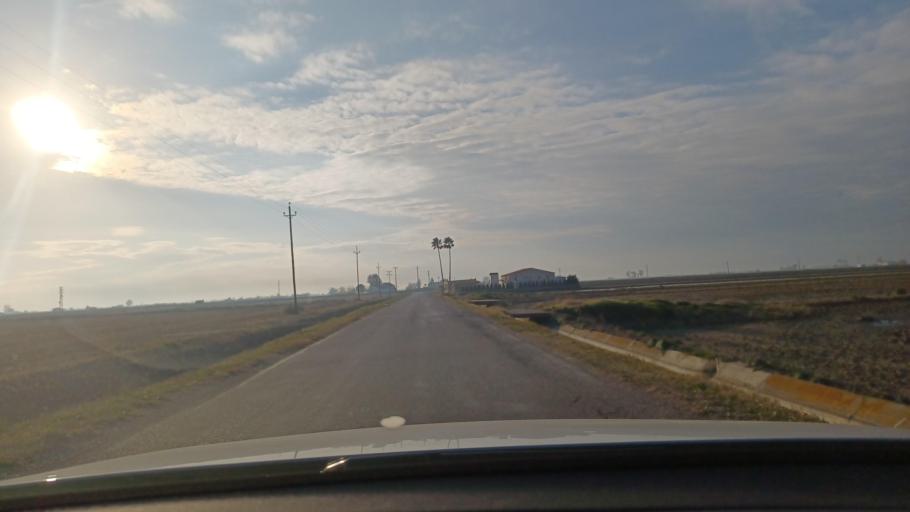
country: ES
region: Catalonia
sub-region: Provincia de Tarragona
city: Deltebre
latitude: 40.6798
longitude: 0.6584
